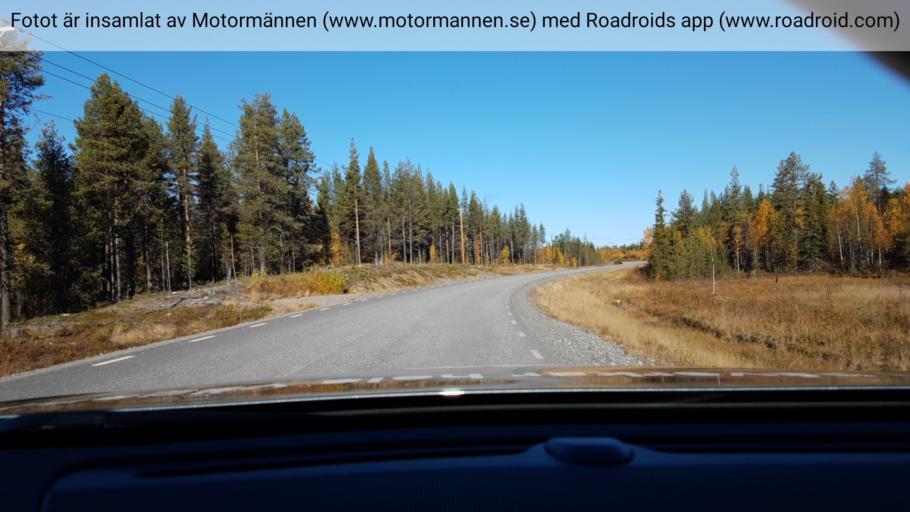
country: SE
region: Norrbotten
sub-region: Gallivare Kommun
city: Gaellivare
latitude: 66.8360
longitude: 21.0406
